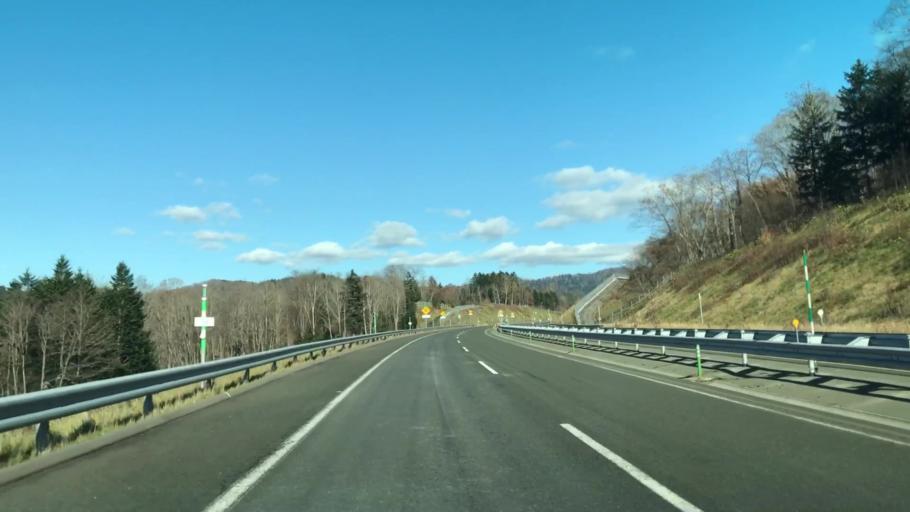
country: JP
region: Hokkaido
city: Shimo-furano
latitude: 42.9371
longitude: 142.2083
